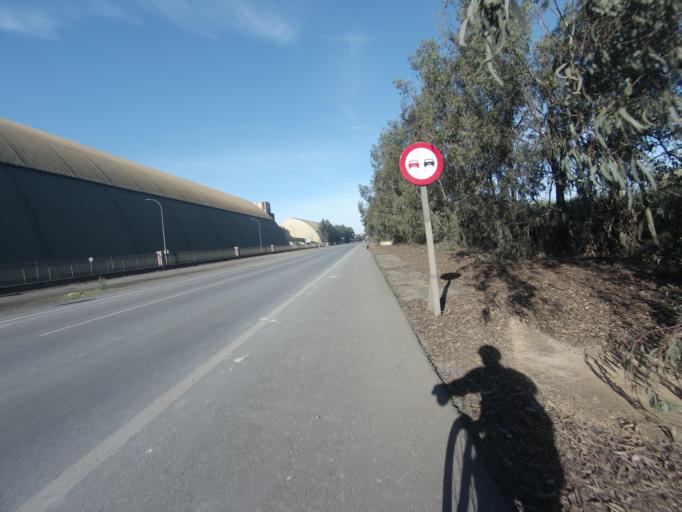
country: ES
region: Andalusia
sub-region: Provincia de Huelva
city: Punta Umbria
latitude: 37.1825
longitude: -6.9229
